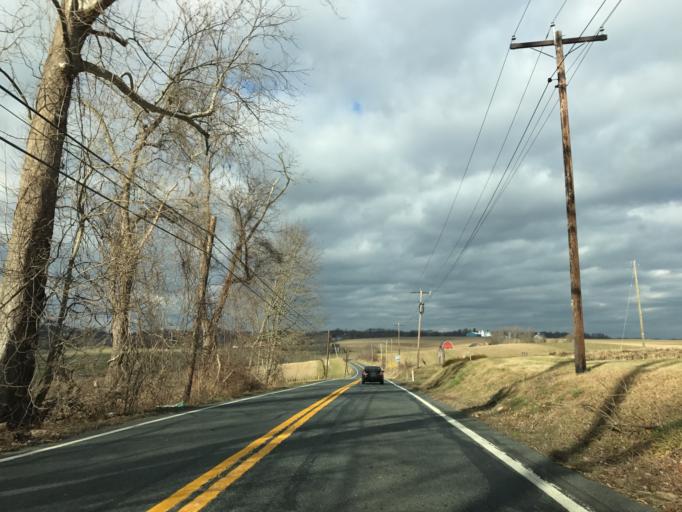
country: US
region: Maryland
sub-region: Harford County
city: South Bel Air
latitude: 39.6060
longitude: -76.2595
